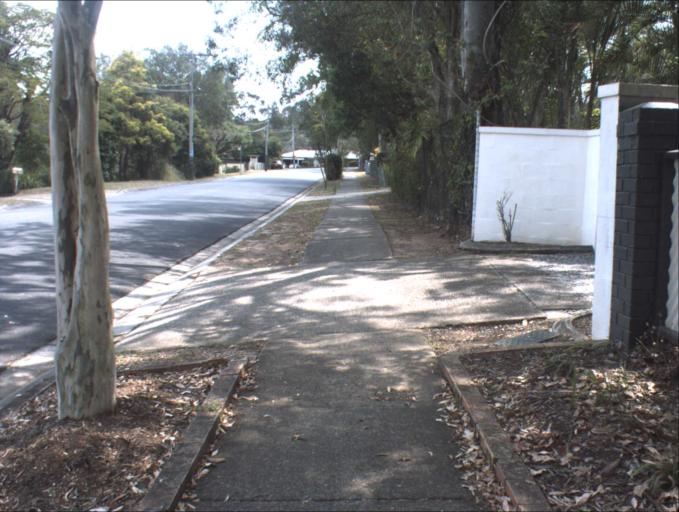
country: AU
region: Queensland
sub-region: Logan
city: Slacks Creek
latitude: -27.6432
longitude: 153.1618
